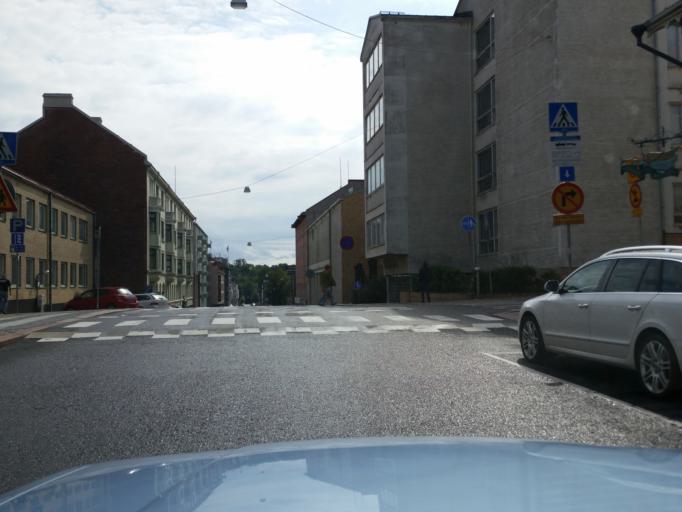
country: FI
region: Varsinais-Suomi
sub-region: Turku
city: Turku
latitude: 60.4546
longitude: 22.2643
